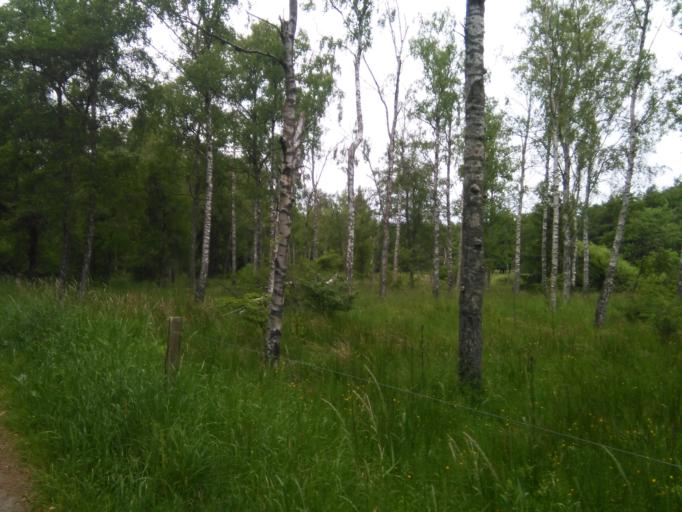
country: DK
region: Capital Region
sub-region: Bornholm Kommune
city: Akirkeby
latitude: 55.1124
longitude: 14.9414
